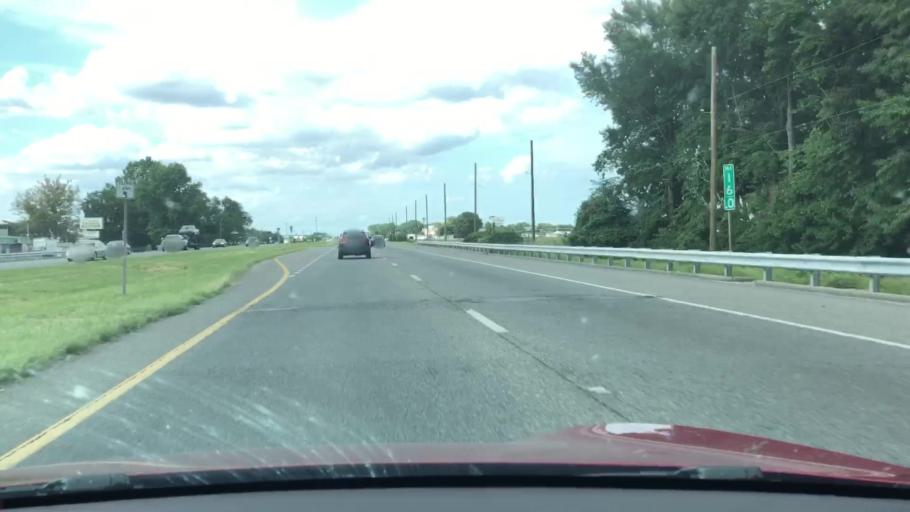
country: US
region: Delaware
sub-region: Sussex County
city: Seaford
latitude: 38.6802
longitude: -75.5915
